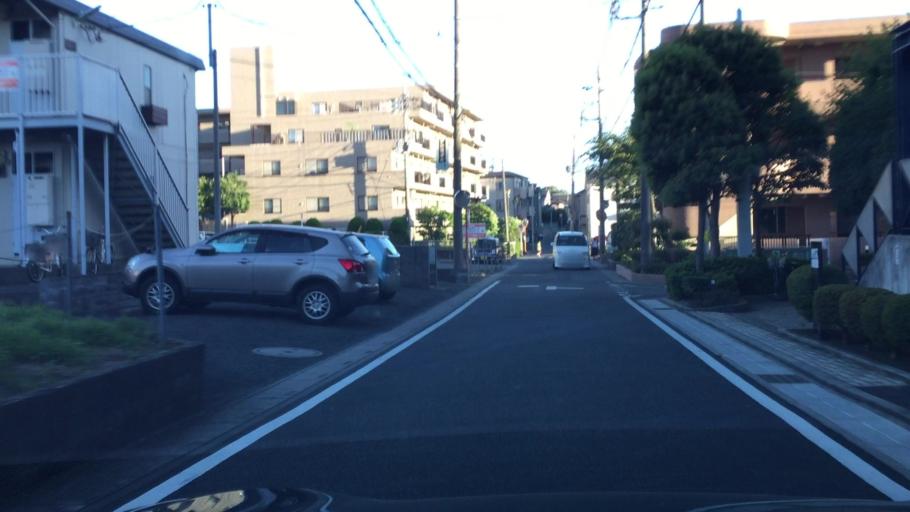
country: JP
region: Saitama
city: Ageoshimo
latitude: 35.9342
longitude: 139.6010
